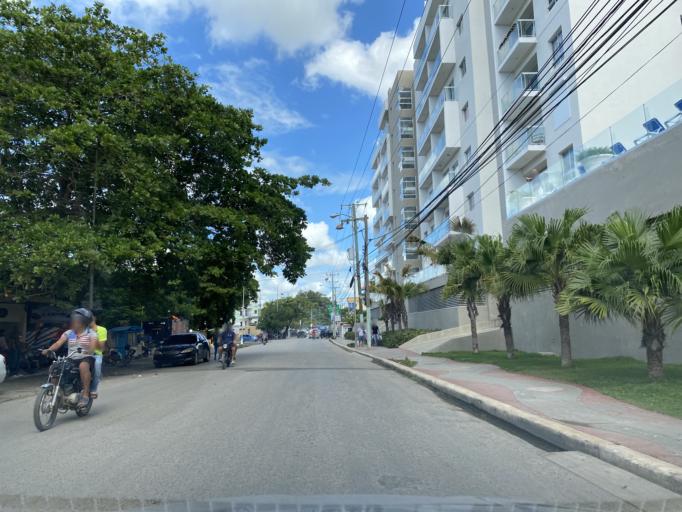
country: DO
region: Santo Domingo
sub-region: Santo Domingo
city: Boca Chica
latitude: 18.4509
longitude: -69.6057
